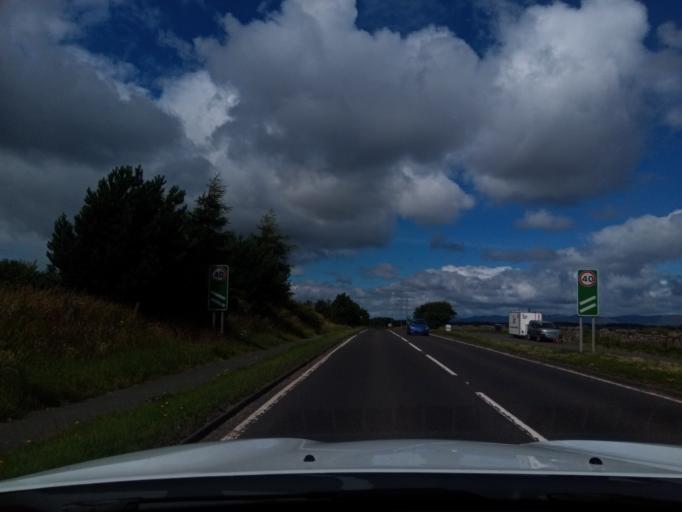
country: GB
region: Scotland
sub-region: Fife
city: Cairneyhill
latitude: 56.0476
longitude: -3.5222
